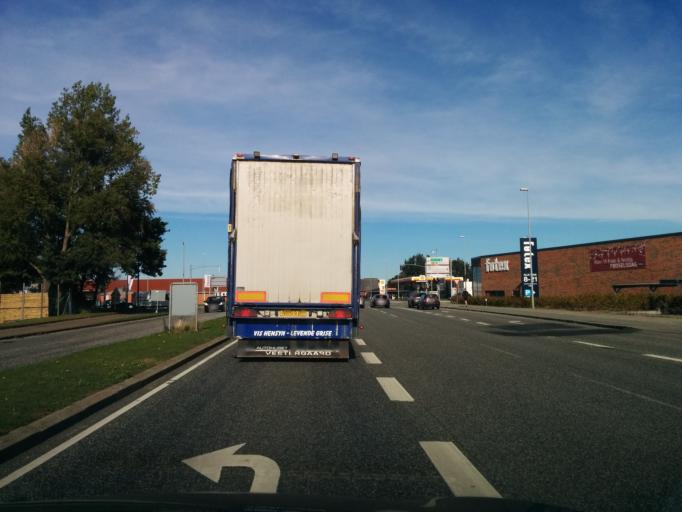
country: DK
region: South Denmark
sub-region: Kolding Kommune
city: Kolding
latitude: 55.4698
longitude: 9.4711
